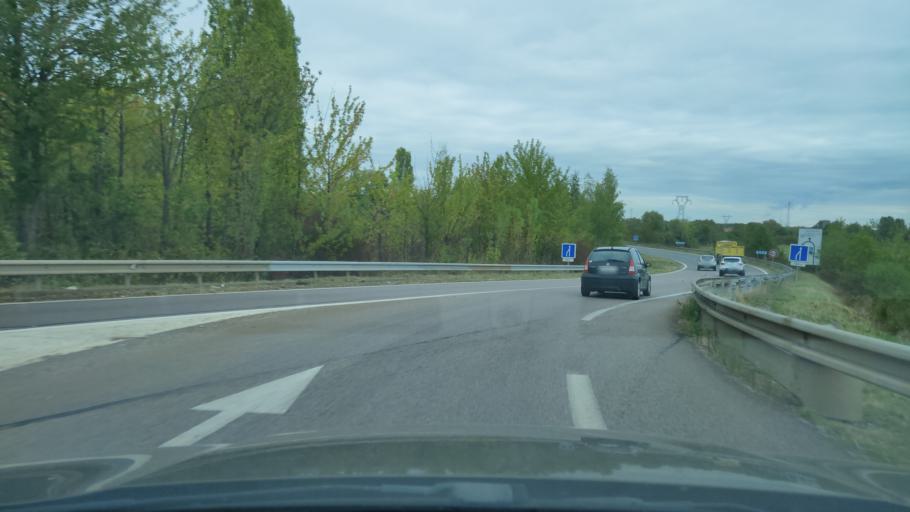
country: FR
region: Lorraine
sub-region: Departement de la Moselle
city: Maizieres-les-Metz
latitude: 49.1986
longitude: 6.1459
